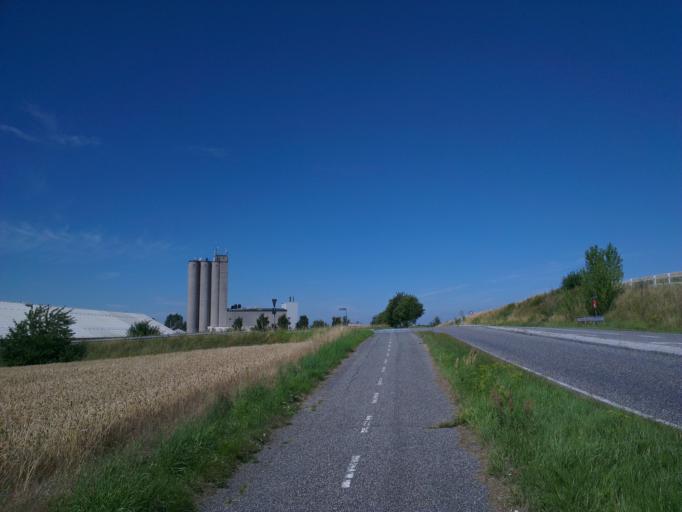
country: DK
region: Capital Region
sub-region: Frederikssund Kommune
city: Slangerup
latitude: 55.8321
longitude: 12.1857
